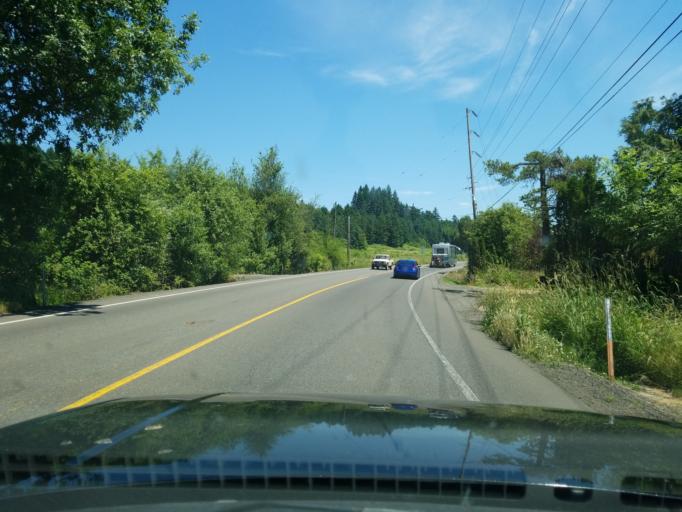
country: US
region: Oregon
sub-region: Yamhill County
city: Yamhill
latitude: 45.3938
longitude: -123.1358
